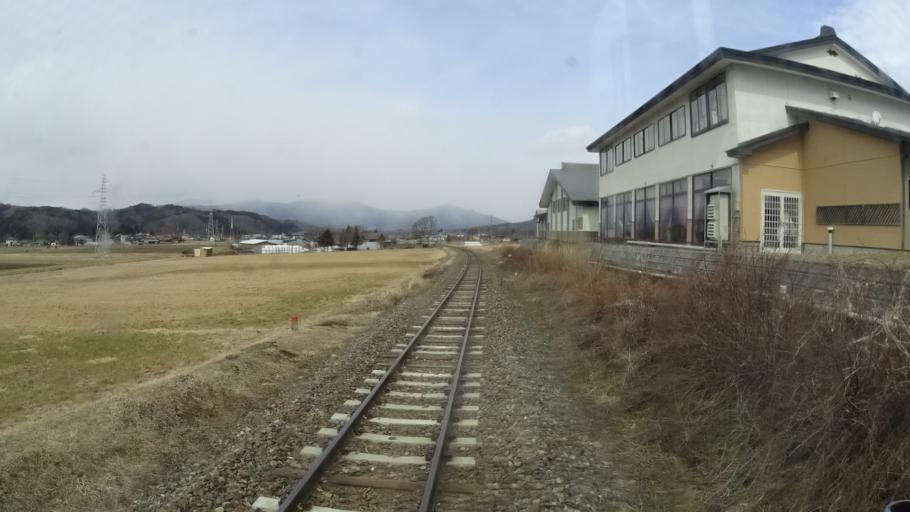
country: JP
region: Iwate
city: Tono
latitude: 39.3055
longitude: 141.5738
